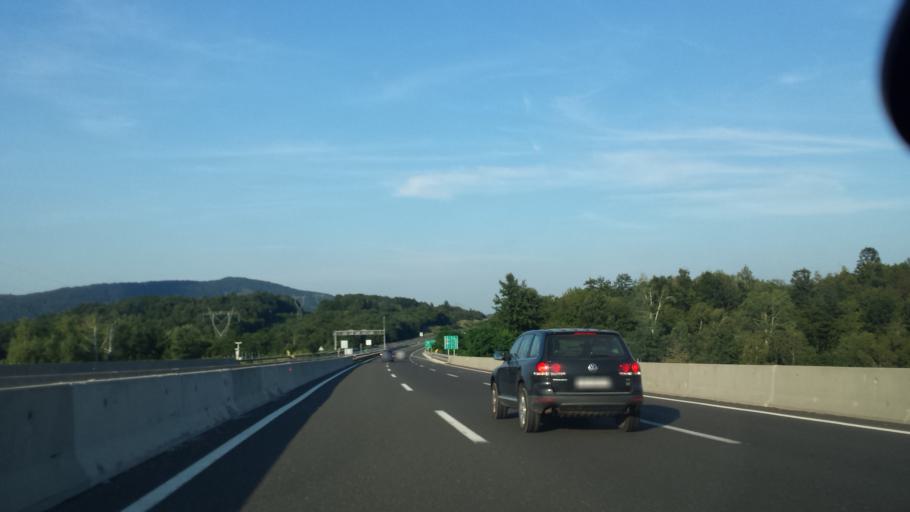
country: HR
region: Karlovacka
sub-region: Grad Ogulin
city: Ogulin
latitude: 45.3993
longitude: 15.2152
